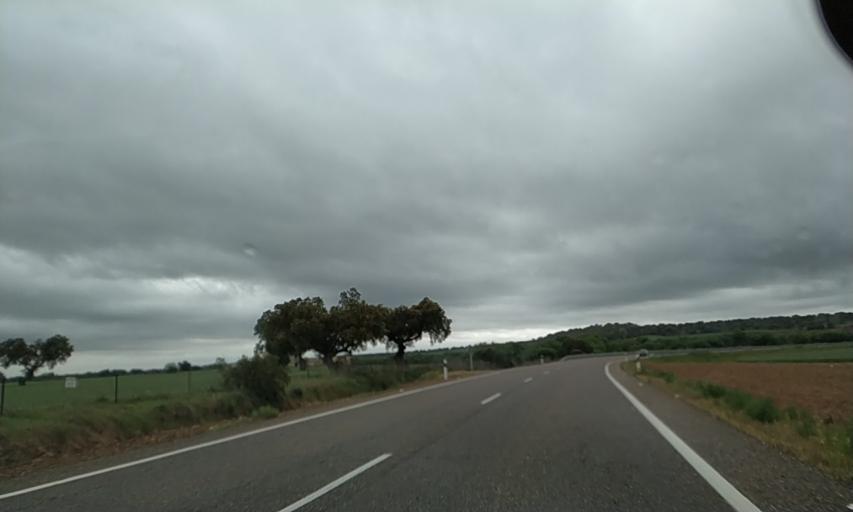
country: ES
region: Extremadura
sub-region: Provincia de Badajoz
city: La Roca de la Sierra
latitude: 39.0589
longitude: -6.7706
